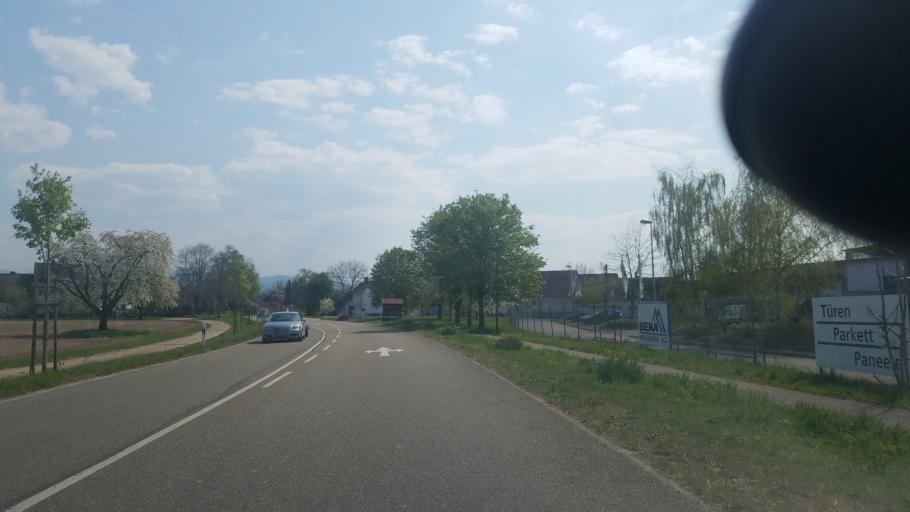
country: DE
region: Baden-Wuerttemberg
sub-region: Freiburg Region
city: Achern
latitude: 48.6357
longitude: 8.0426
